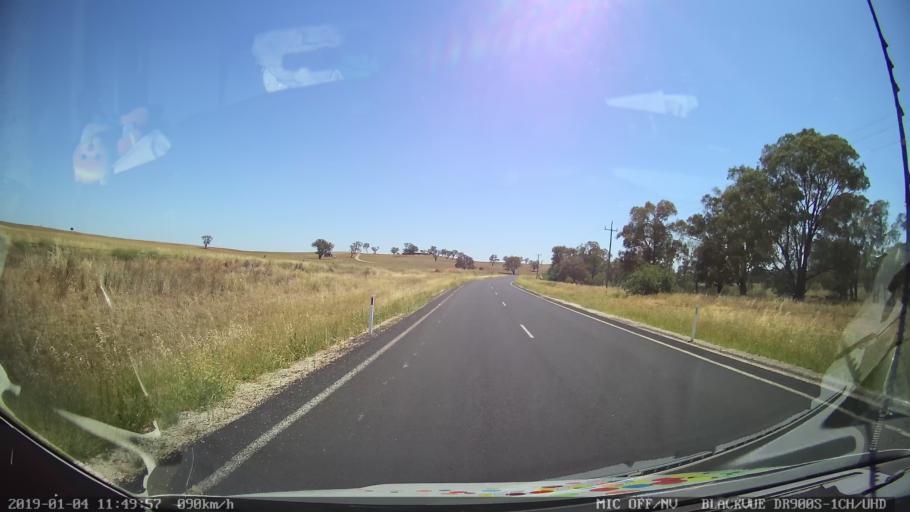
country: AU
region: New South Wales
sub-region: Cabonne
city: Molong
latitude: -32.9124
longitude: 148.7552
